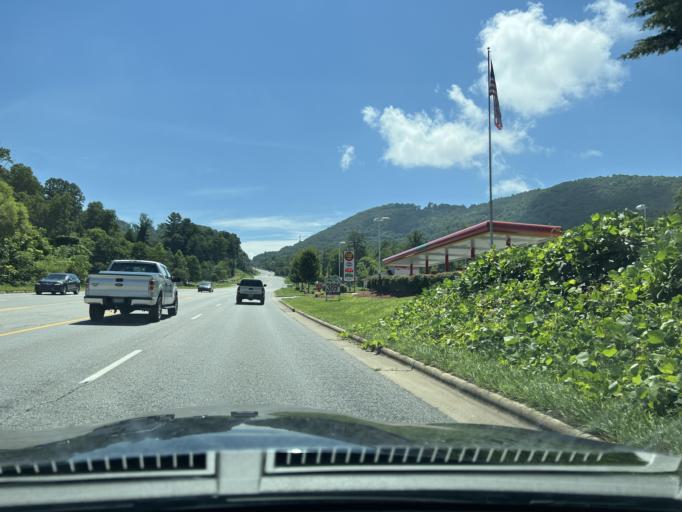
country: US
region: North Carolina
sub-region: Buncombe County
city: Biltmore Forest
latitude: 35.5507
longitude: -82.4710
